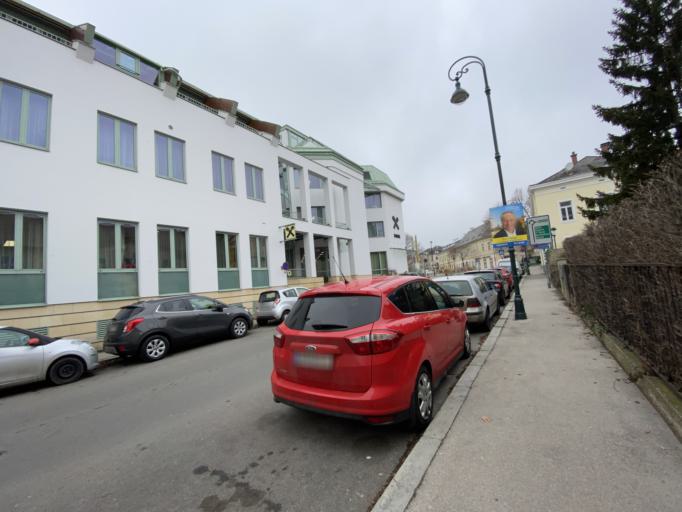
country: AT
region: Lower Austria
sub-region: Politischer Bezirk Baden
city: Baden
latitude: 48.0052
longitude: 16.2326
